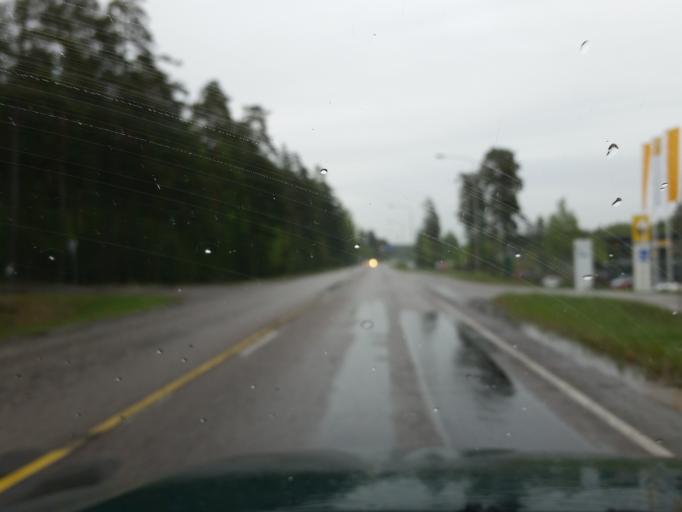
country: FI
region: Uusimaa
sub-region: Helsinki
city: Lohja
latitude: 60.2865
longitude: 24.1751
